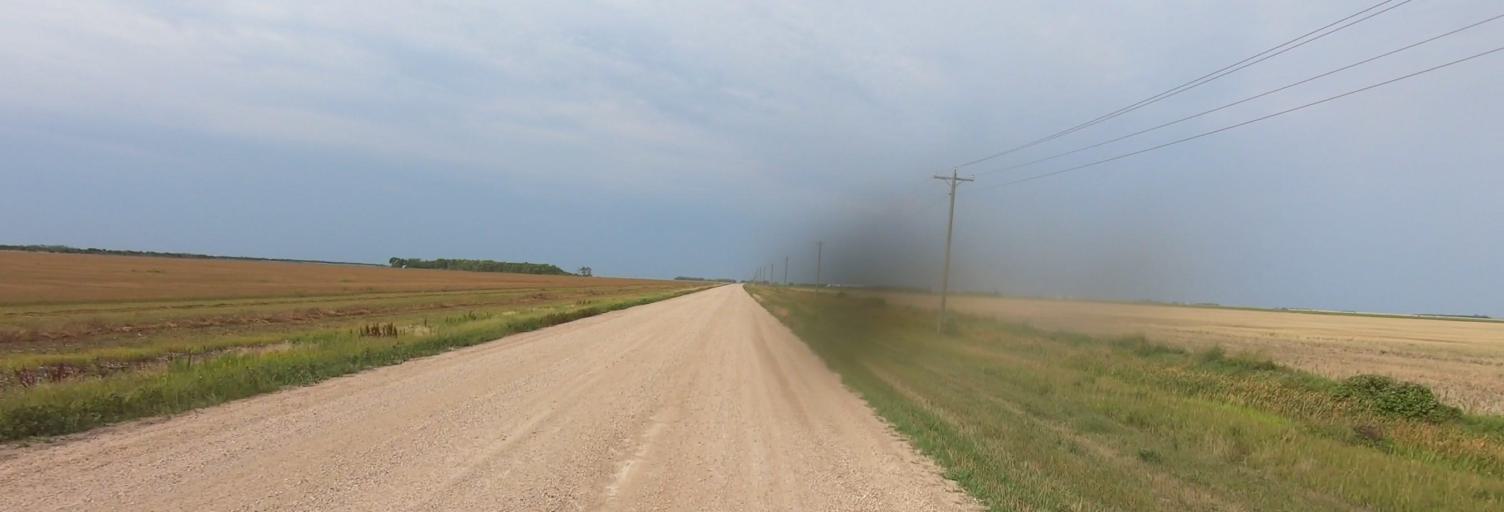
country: CA
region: Manitoba
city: Morris
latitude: 49.5764
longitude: -97.3039
